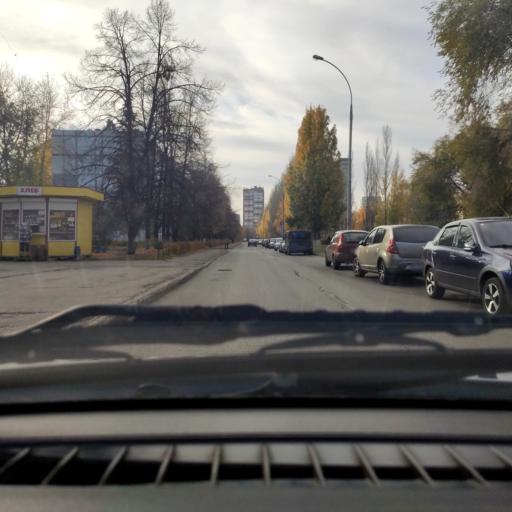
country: RU
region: Samara
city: Tol'yatti
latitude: 53.5310
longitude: 49.3045
